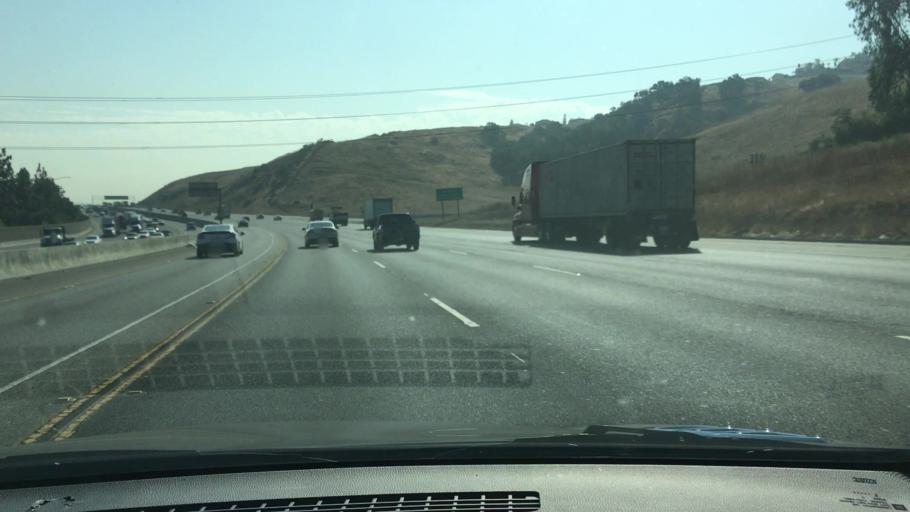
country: US
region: California
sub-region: San Bernardino County
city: Chino Hills
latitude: 34.0235
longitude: -117.7688
